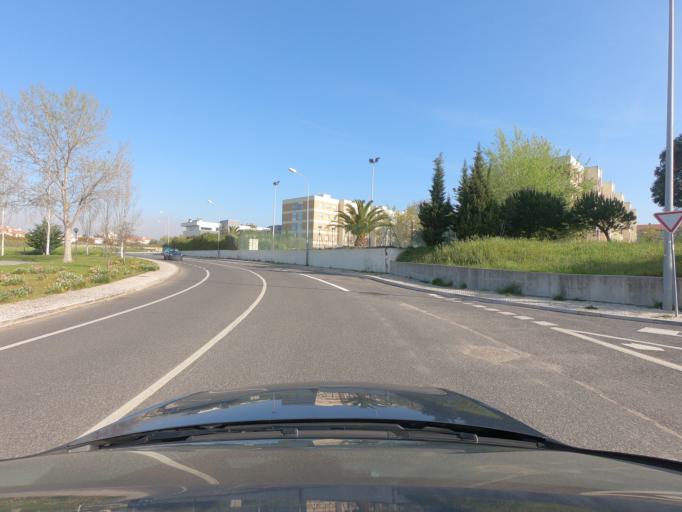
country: PT
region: Lisbon
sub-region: Oeiras
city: Carcavelos
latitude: 38.6815
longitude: -9.3232
